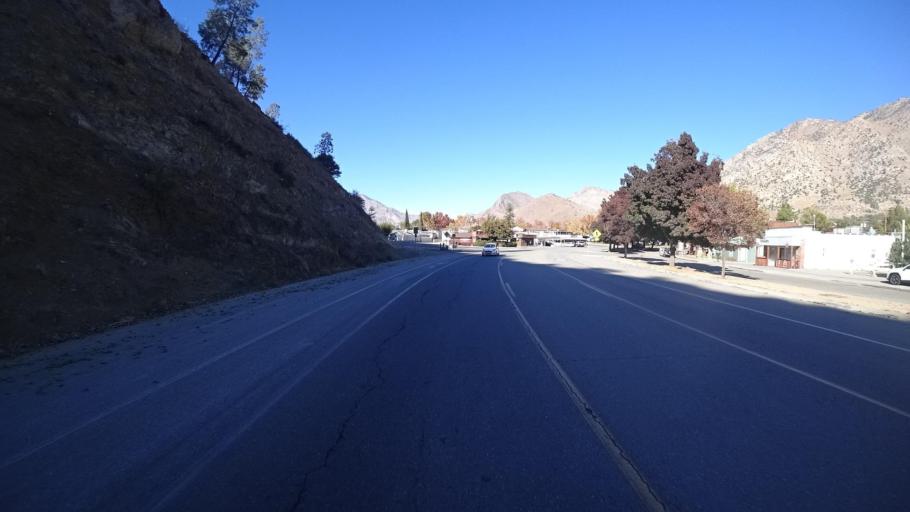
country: US
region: California
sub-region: Kern County
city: Kernville
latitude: 35.7531
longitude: -118.4246
